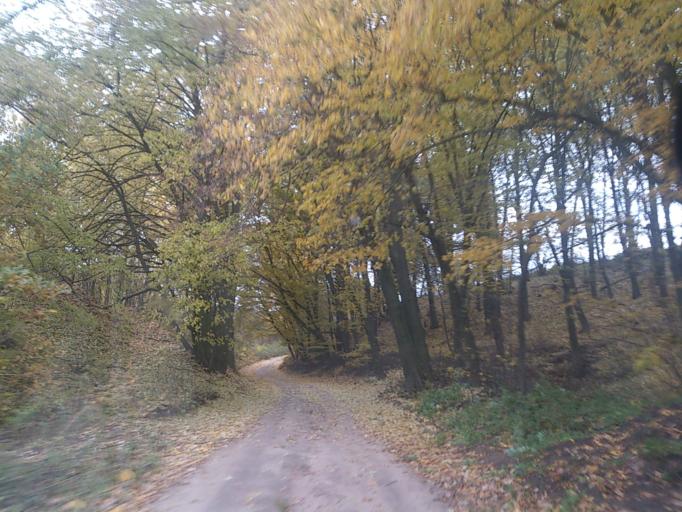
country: PL
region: Kujawsko-Pomorskie
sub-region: Powiat golubsko-dobrzynski
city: Golub-Dobrzyn
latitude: 53.1250
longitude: 19.0627
